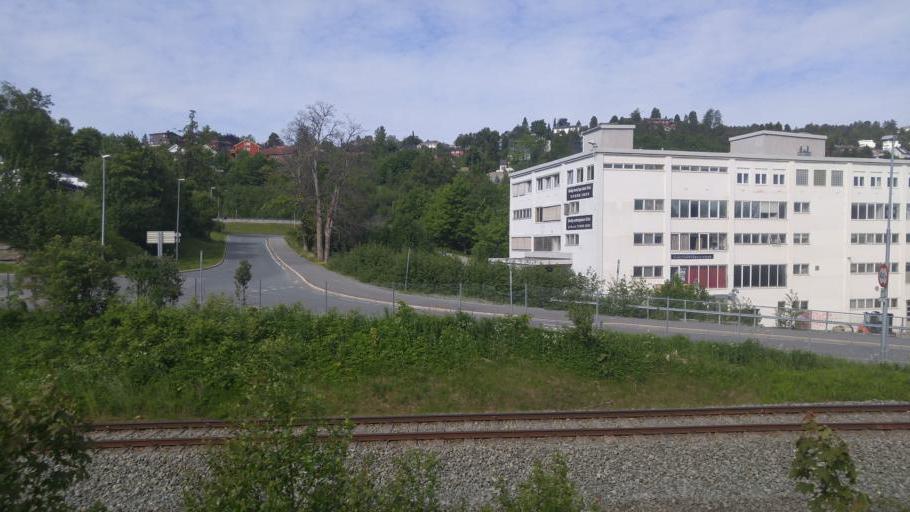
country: NO
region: Sor-Trondelag
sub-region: Trondheim
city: Trondheim
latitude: 63.4167
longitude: 10.3834
